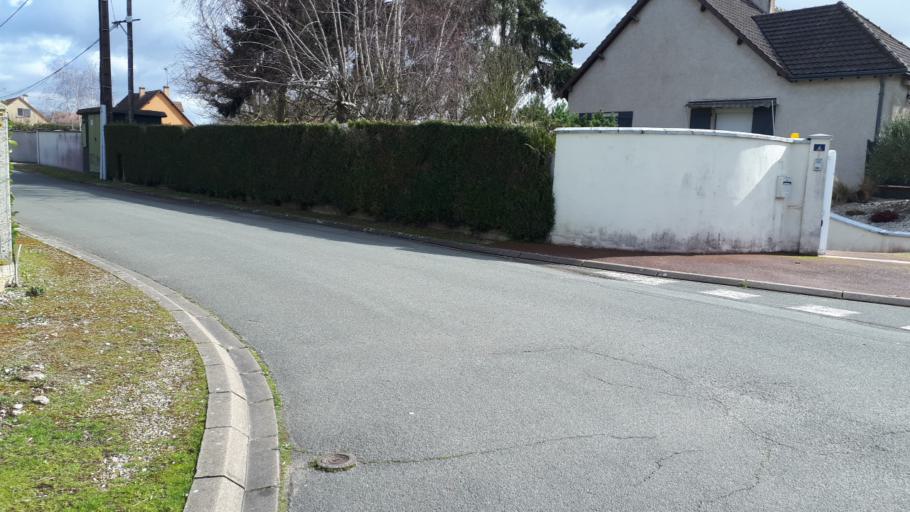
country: FR
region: Centre
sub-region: Departement du Loir-et-Cher
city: Villiers-sur-Loir
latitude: 47.7909
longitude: 0.9988
